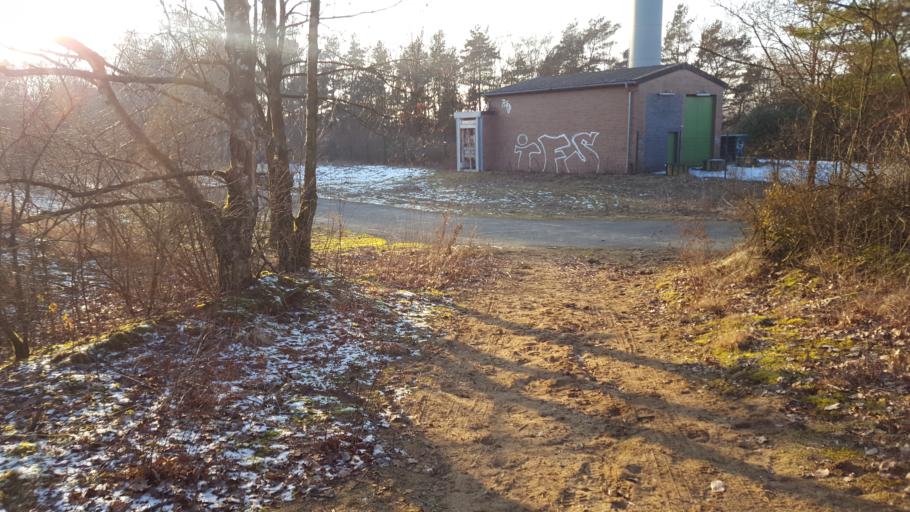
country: DE
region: North Rhine-Westphalia
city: Oer-Erkenschwick
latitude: 51.6658
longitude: 7.2565
